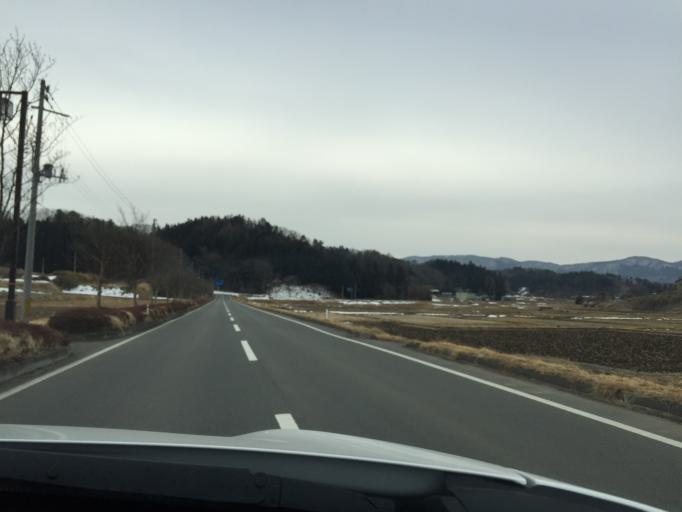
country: JP
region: Fukushima
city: Funehikimachi-funehiki
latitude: 37.4011
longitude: 140.6161
